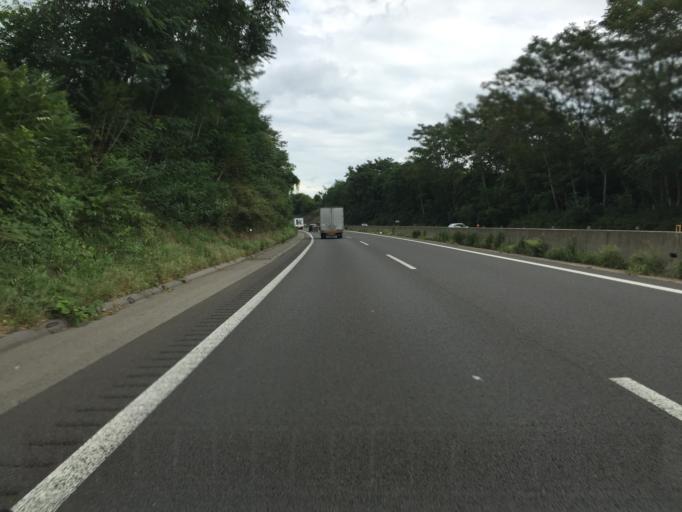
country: JP
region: Fukushima
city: Hobaramachi
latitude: 37.8403
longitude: 140.5009
